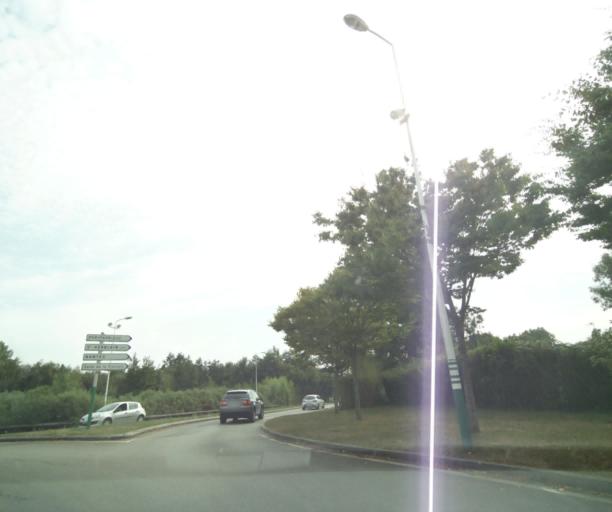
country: FR
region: Pays de la Loire
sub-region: Departement de la Loire-Atlantique
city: Saint-Herblain
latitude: 47.2147
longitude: -1.6385
